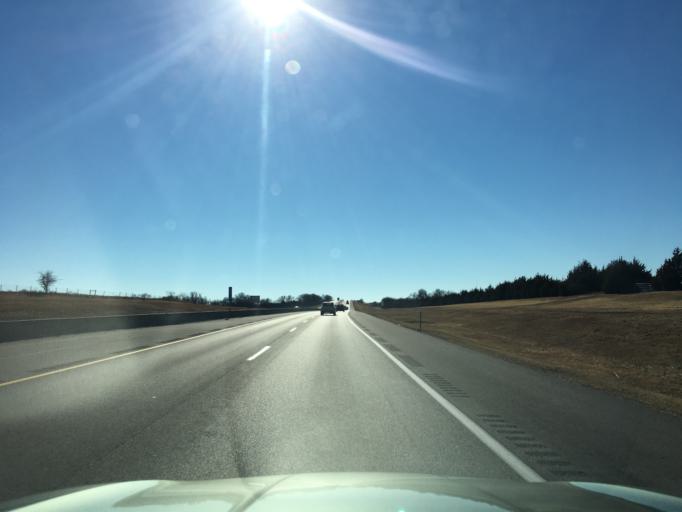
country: US
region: Kansas
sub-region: Sumner County
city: Belle Plaine
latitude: 37.3594
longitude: -97.3223
